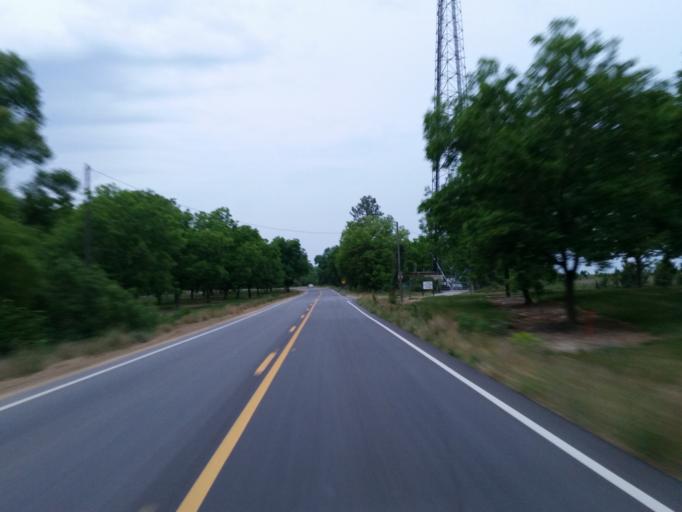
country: US
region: Georgia
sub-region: Turner County
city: Ashburn
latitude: 31.7974
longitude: -83.7103
